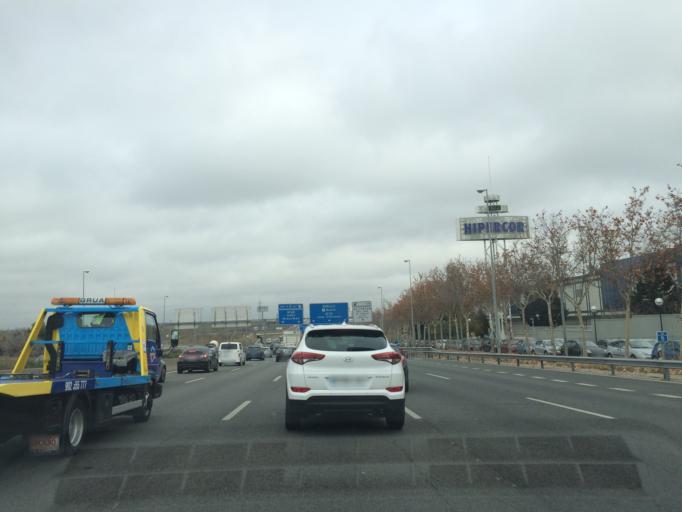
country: ES
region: Madrid
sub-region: Provincia de Madrid
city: Alcorcon
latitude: 40.3579
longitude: -3.8183
